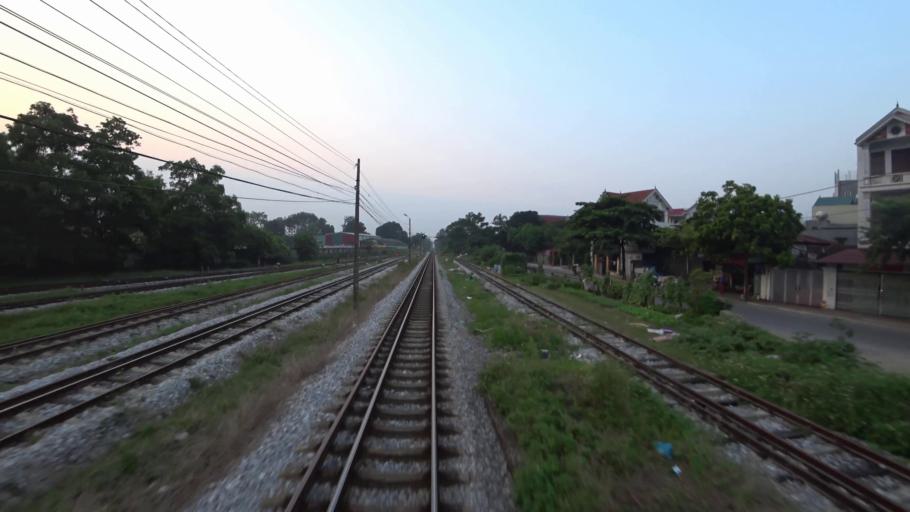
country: VN
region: Ha Noi
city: Dong Anh
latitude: 21.1402
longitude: 105.8662
